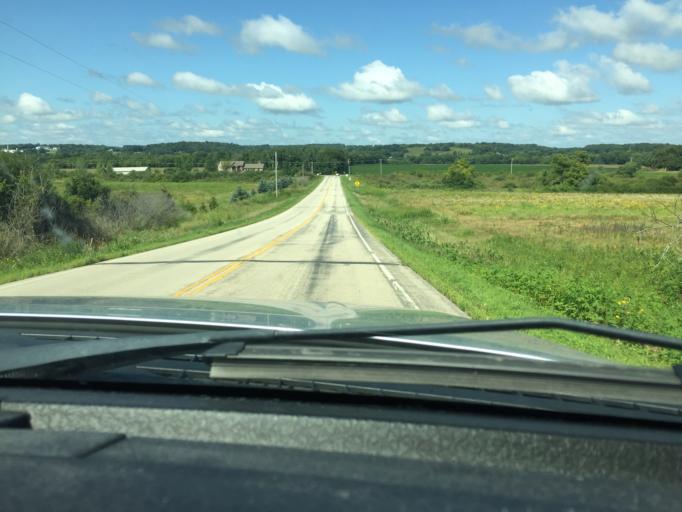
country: US
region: Minnesota
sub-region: Olmsted County
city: Rochester
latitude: 43.9640
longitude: -92.5528
